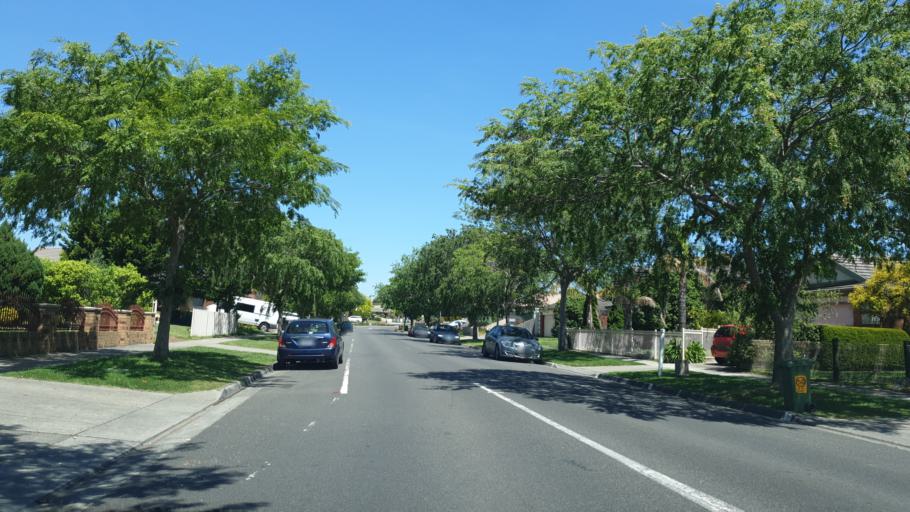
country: AU
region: Victoria
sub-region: Casey
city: Narre Warren South
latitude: -38.0587
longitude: 145.2979
